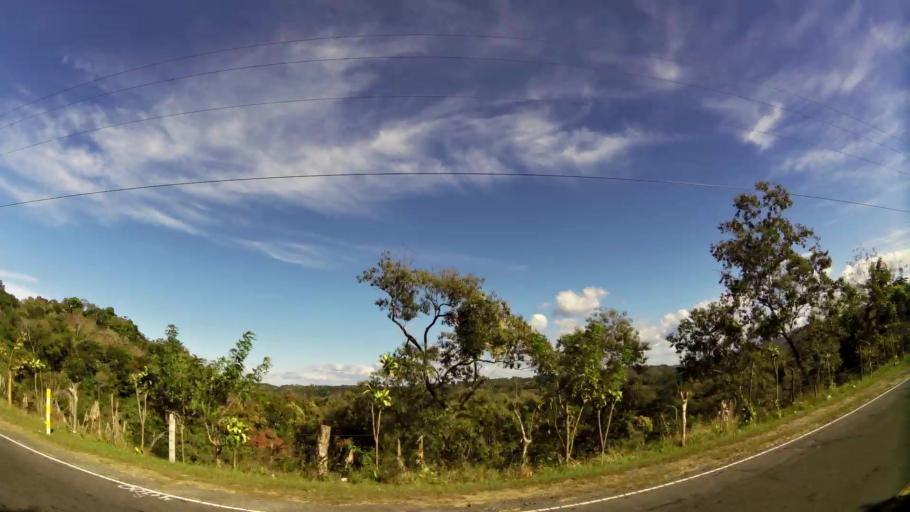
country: SV
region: Cuscatlan
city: Tenancingo
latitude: 13.8352
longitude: -89.0279
